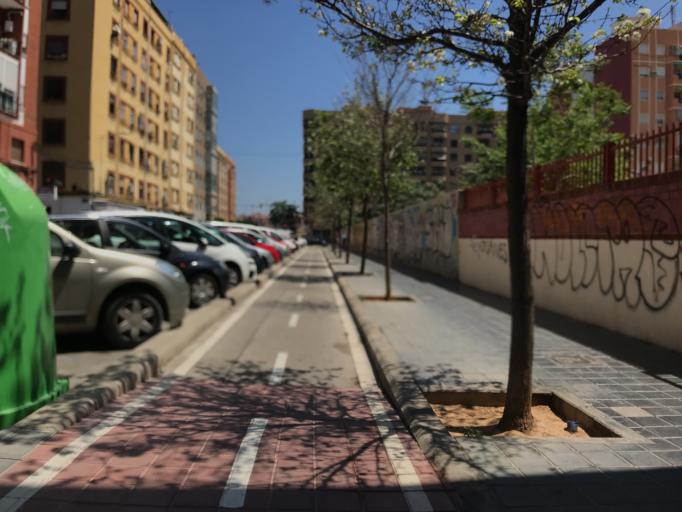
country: ES
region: Valencia
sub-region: Provincia de Valencia
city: Valencia
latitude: 39.4564
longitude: -0.3851
